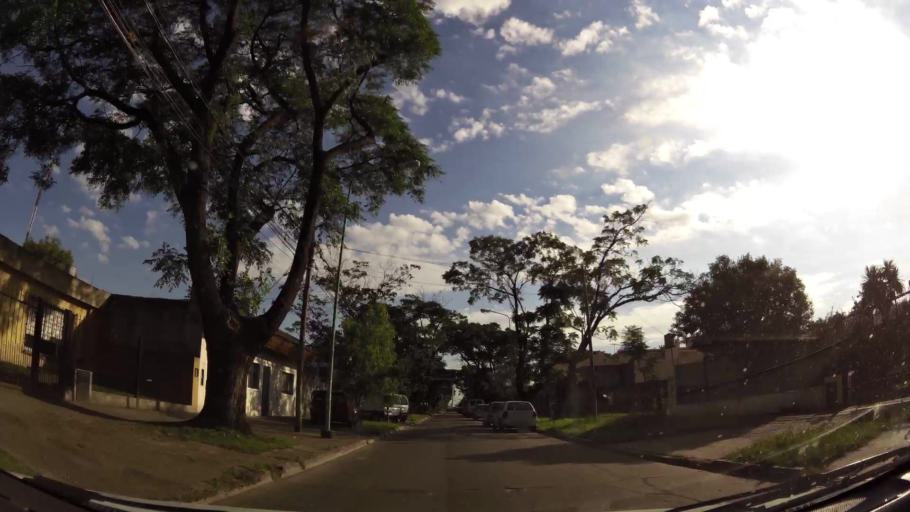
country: AR
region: Buenos Aires
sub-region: Partido de Merlo
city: Merlo
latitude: -34.6714
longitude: -58.7228
